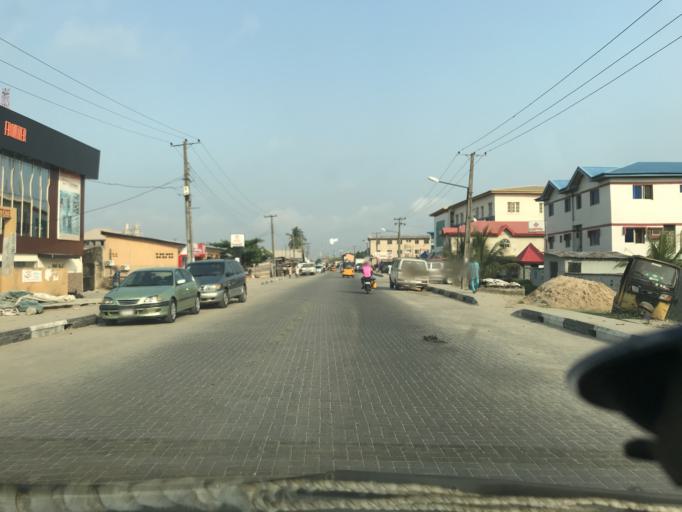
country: NG
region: Lagos
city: Ikorodu
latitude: 6.5016
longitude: 3.5834
